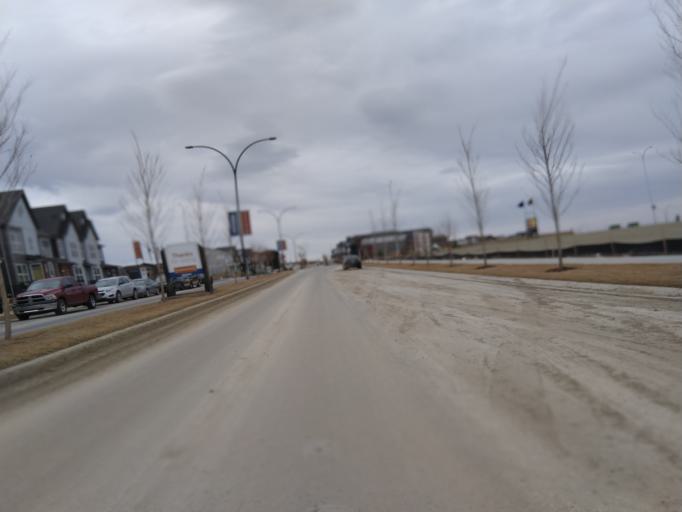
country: CA
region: Alberta
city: Airdrie
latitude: 51.1824
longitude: -114.0755
